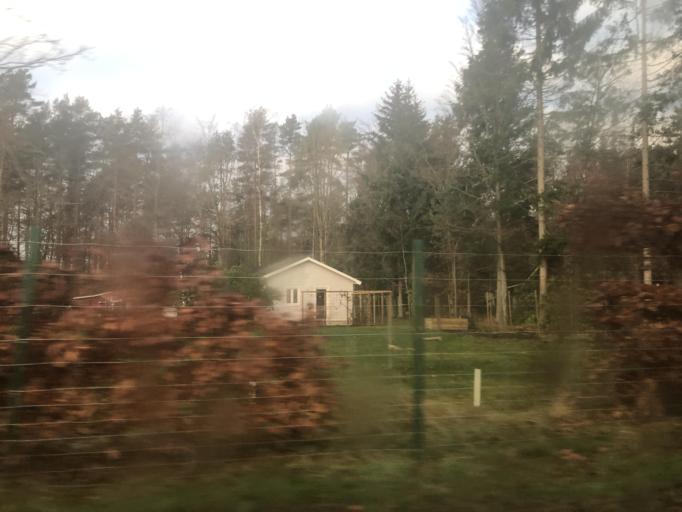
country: SE
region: Skane
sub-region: Sjobo Kommun
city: Blentarp
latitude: 55.6120
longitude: 13.5458
